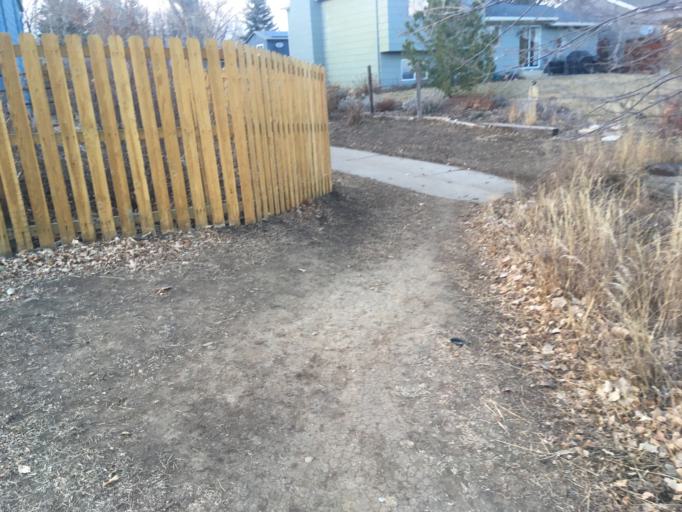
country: US
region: Colorado
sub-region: Boulder County
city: Lafayette
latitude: 40.0041
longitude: -105.0911
